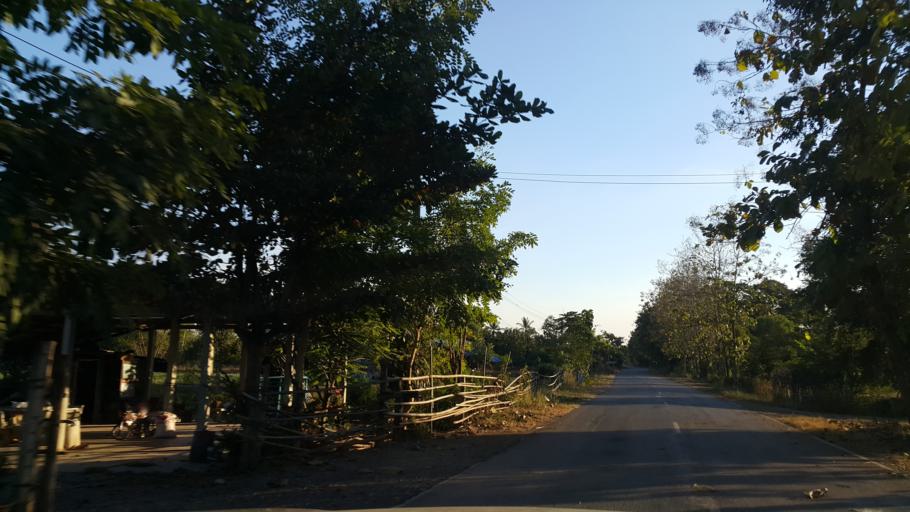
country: TH
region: Sukhothai
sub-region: Amphoe Si Satchanalai
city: Si Satchanalai
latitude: 17.5457
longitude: 99.9032
